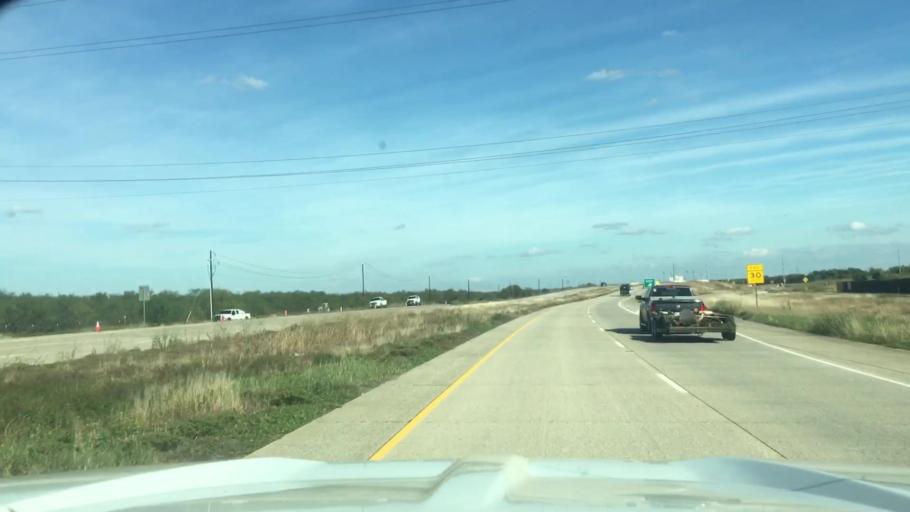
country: US
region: Texas
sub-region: Denton County
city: Denton
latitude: 33.2599
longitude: -97.1372
